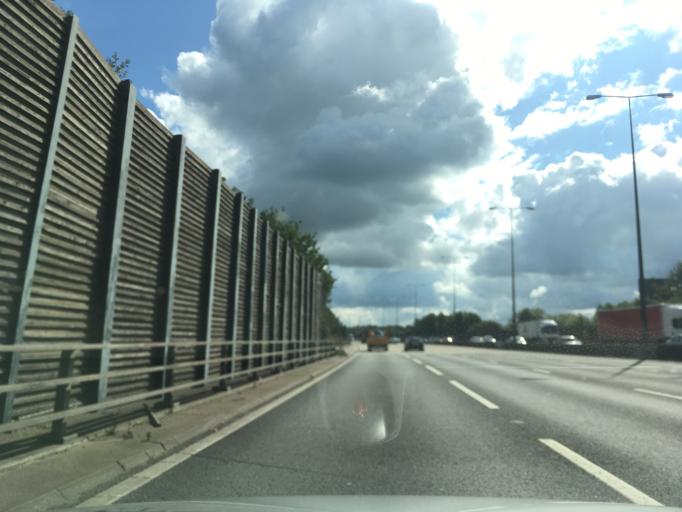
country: GB
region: England
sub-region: Surrey
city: Byfleet
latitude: 51.3294
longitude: -0.4783
